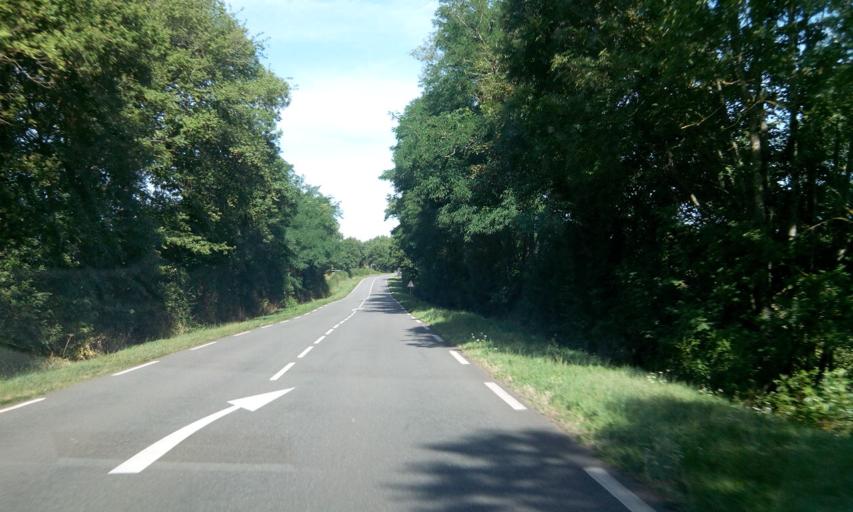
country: FR
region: Poitou-Charentes
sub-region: Departement de la Charente
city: Exideuil
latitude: 45.9528
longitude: 0.7115
